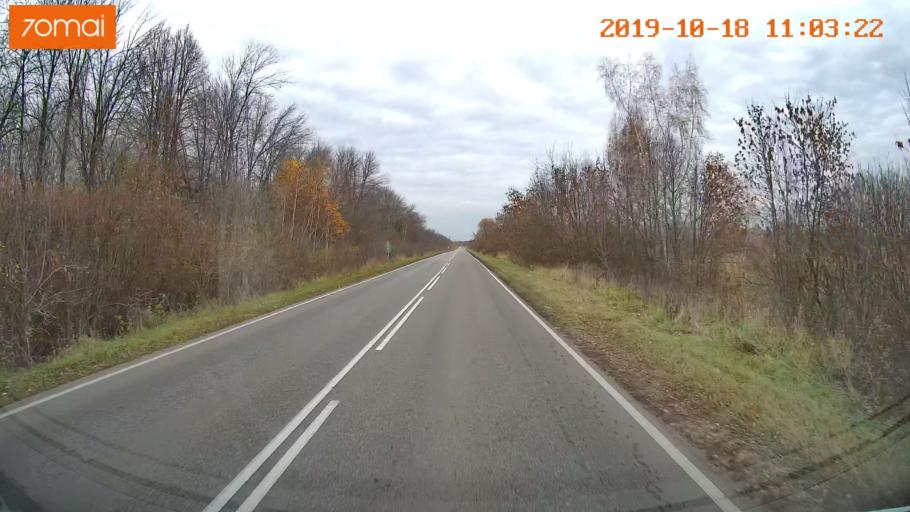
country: RU
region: Tula
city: Yepifan'
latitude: 53.8786
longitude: 38.5484
